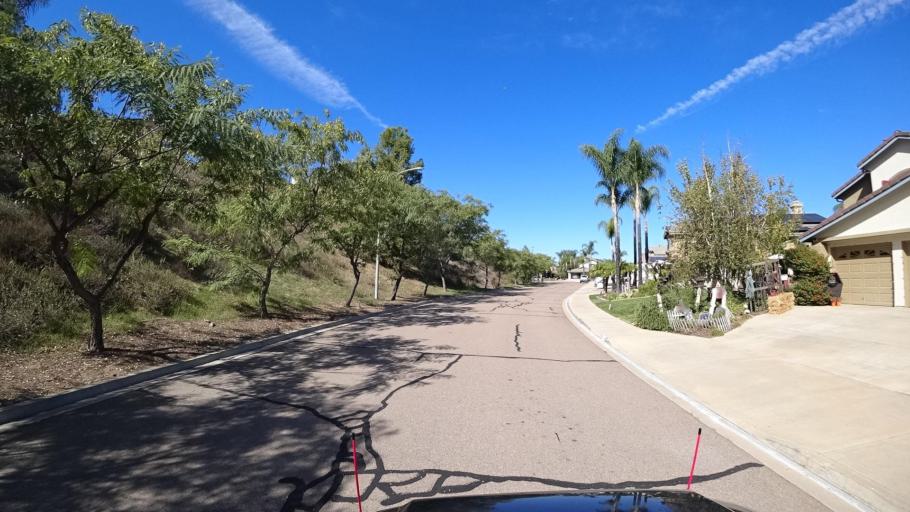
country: US
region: California
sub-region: San Diego County
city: Granite Hills
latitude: 32.8277
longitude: -116.8954
